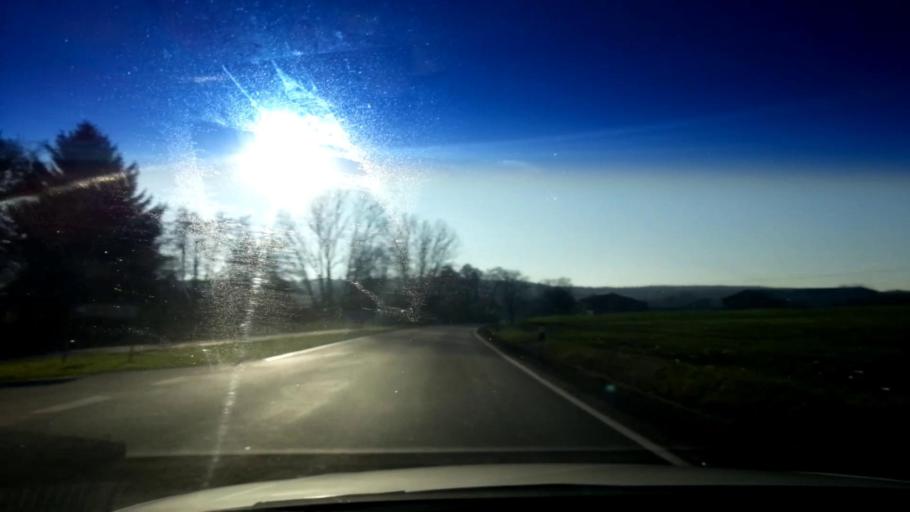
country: DE
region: Bavaria
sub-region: Upper Franconia
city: Litzendorf
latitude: 49.9162
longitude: 10.9974
